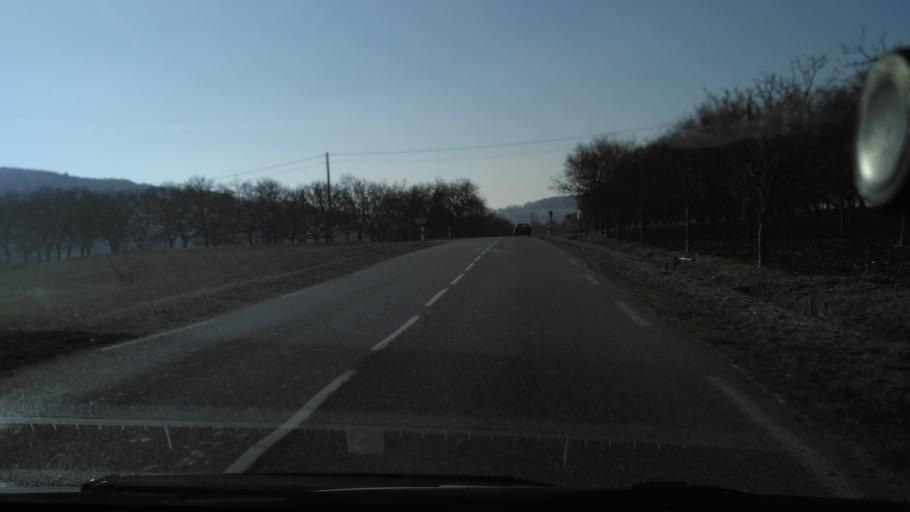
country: FR
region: Rhone-Alpes
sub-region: Departement de la Drome
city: Genissieux
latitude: 45.1404
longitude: 5.1174
